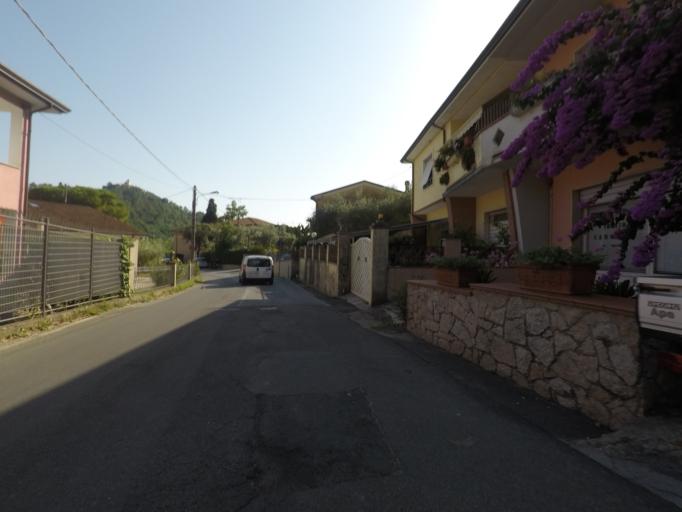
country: IT
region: Liguria
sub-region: Provincia di La Spezia
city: Casano-Dogana-Isola
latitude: 44.0857
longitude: 10.0427
